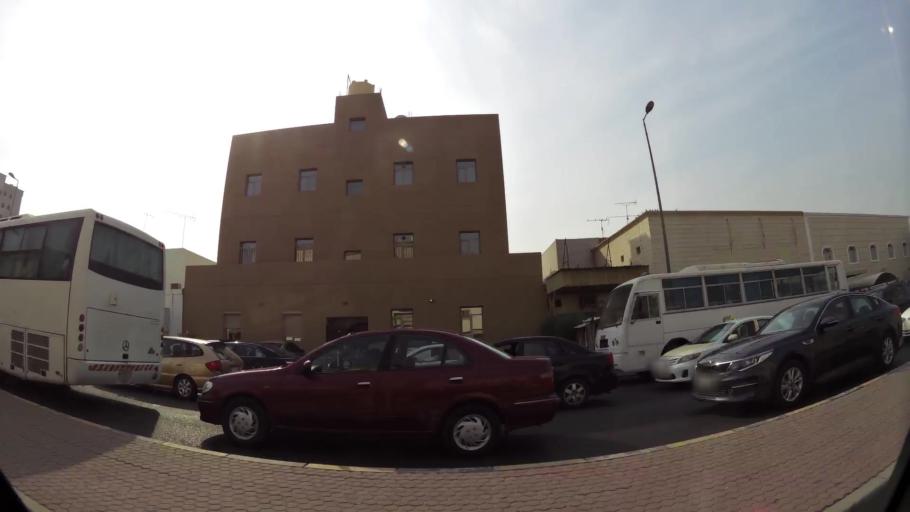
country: KW
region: Al Farwaniyah
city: Al Farwaniyah
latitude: 29.2905
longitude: 47.9546
